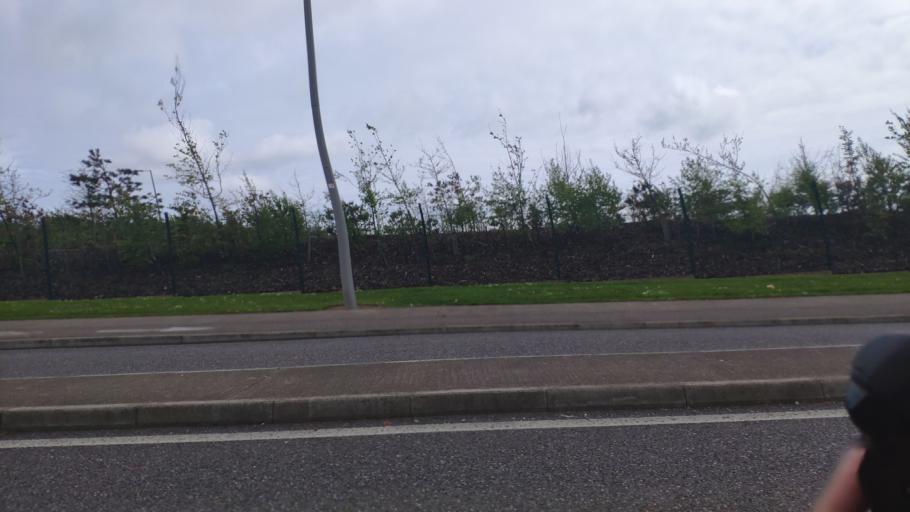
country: IE
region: Munster
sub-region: County Cork
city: Cork
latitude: 51.9073
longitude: -8.5175
